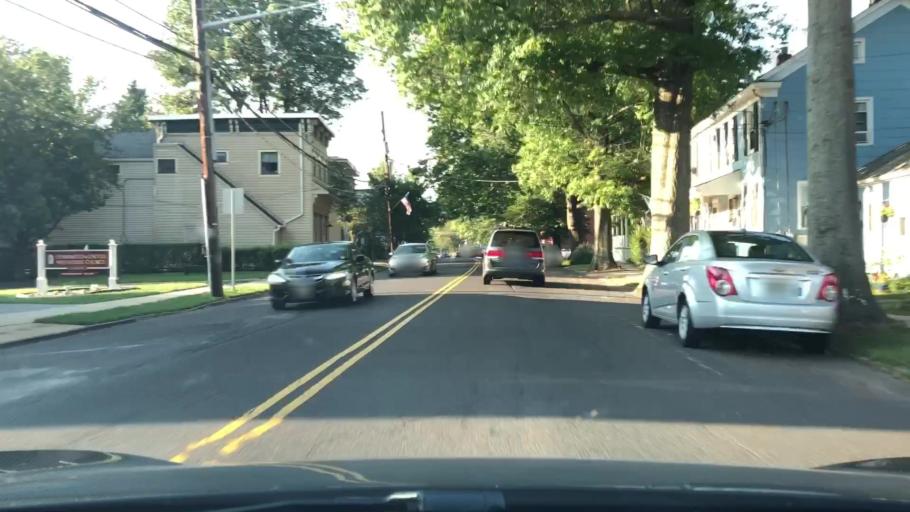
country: US
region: New Jersey
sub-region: Mercer County
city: Pennington
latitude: 40.3261
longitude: -74.7907
